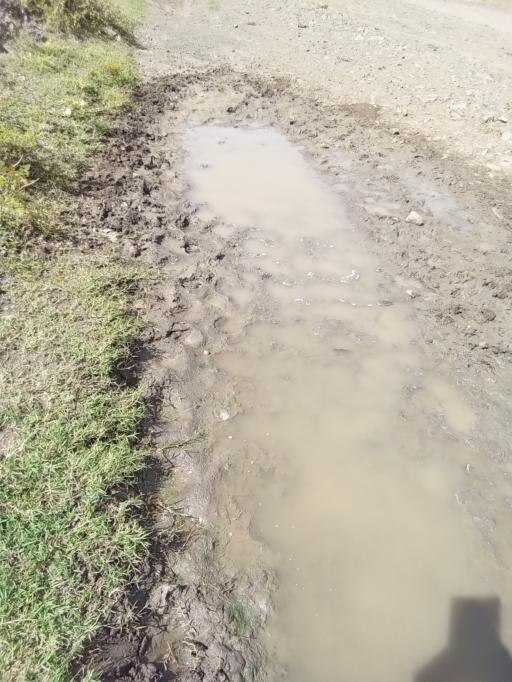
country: KE
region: Homa Bay
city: Homa Bay
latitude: -0.4504
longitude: 34.2007
